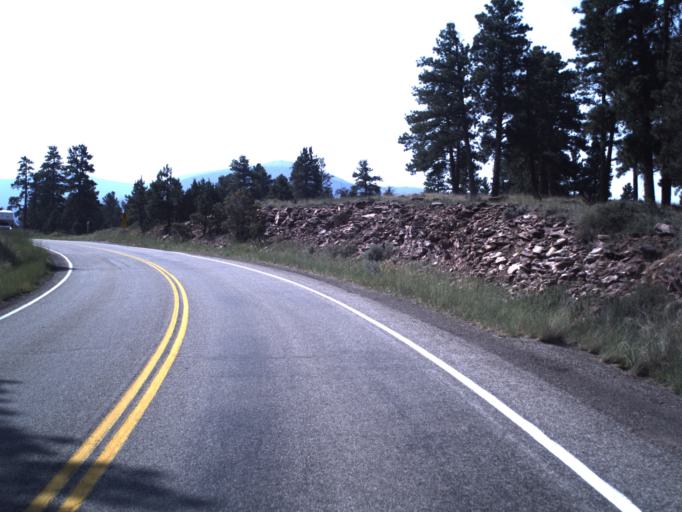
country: US
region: Utah
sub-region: Daggett County
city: Manila
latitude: 40.8919
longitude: -109.4588
